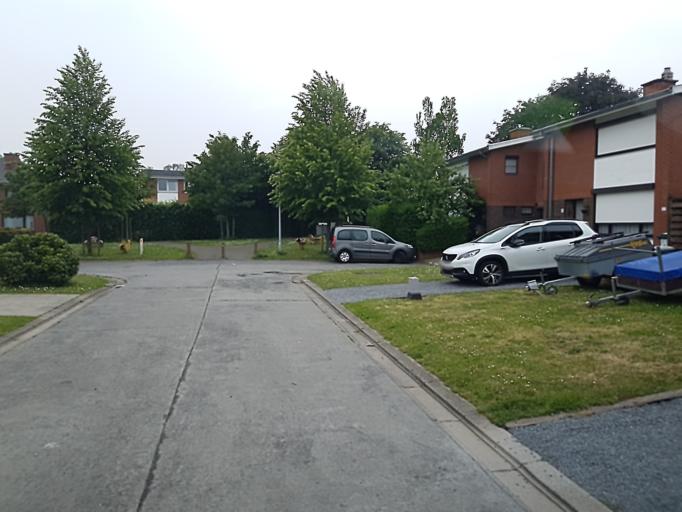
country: BE
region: Flanders
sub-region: Provincie West-Vlaanderen
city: Zonnebeke
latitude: 50.8363
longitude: 2.9921
